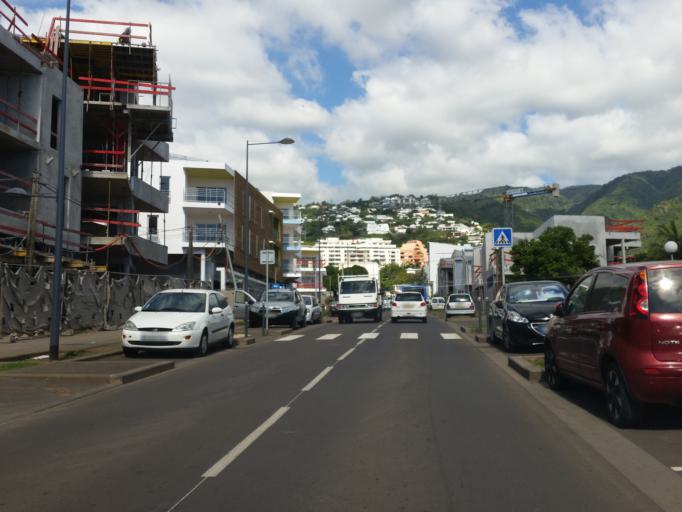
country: RE
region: Reunion
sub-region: Reunion
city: Saint-Denis
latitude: -20.8942
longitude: 55.4602
